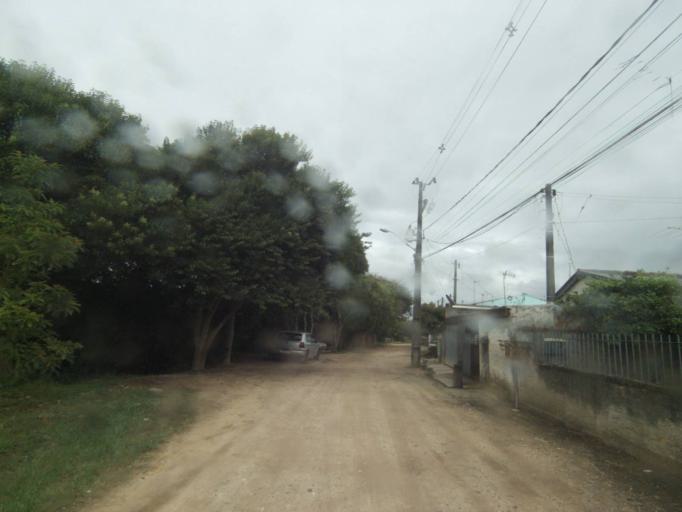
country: BR
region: Parana
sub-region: Curitiba
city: Curitiba
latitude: -25.4860
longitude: -49.3070
